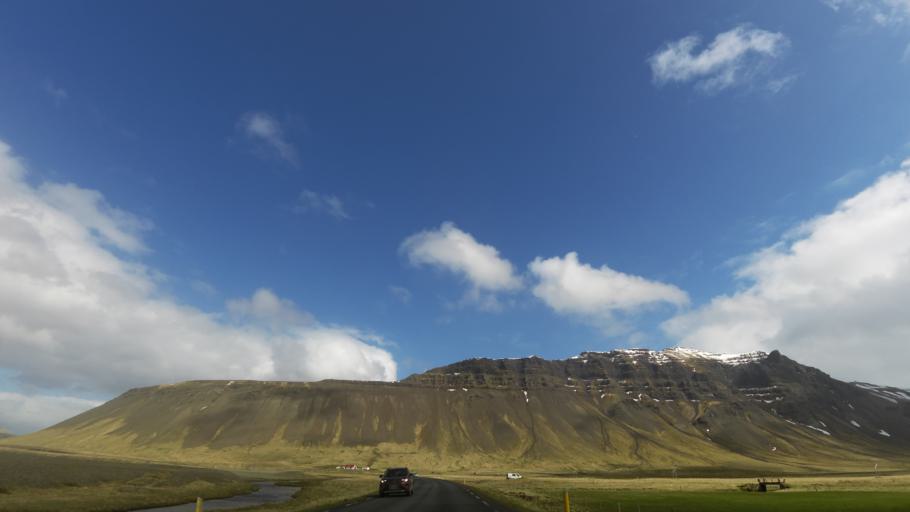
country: IS
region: West
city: Olafsvik
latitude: 64.9224
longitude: -23.2256
